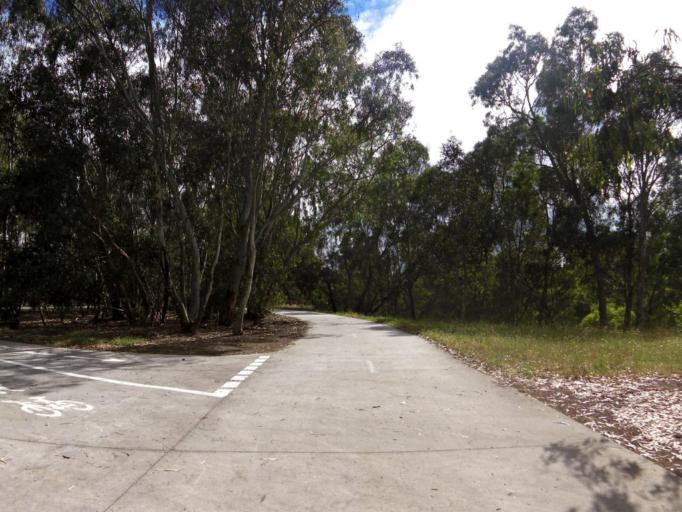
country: AU
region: Victoria
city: Heidelberg West
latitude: -37.7611
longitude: 145.0281
